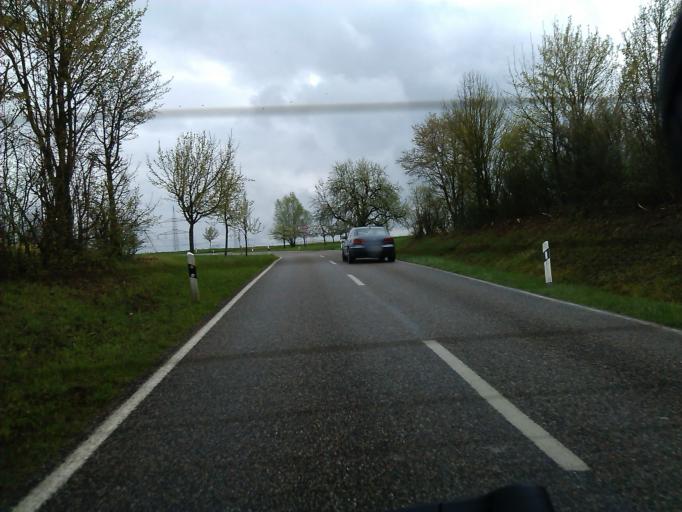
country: DE
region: Baden-Wuerttemberg
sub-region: Regierungsbezirk Stuttgart
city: Bad Rappenau
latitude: 49.2532
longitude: 9.1128
